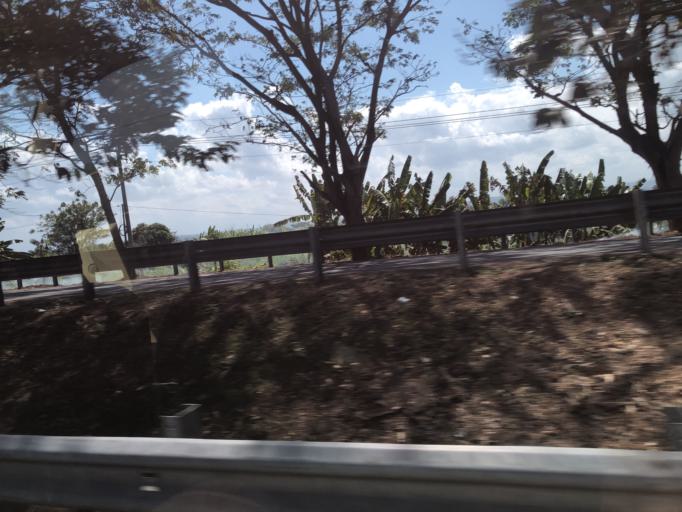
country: ID
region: Bali
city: Semarapura
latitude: -8.5692
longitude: 115.4076
